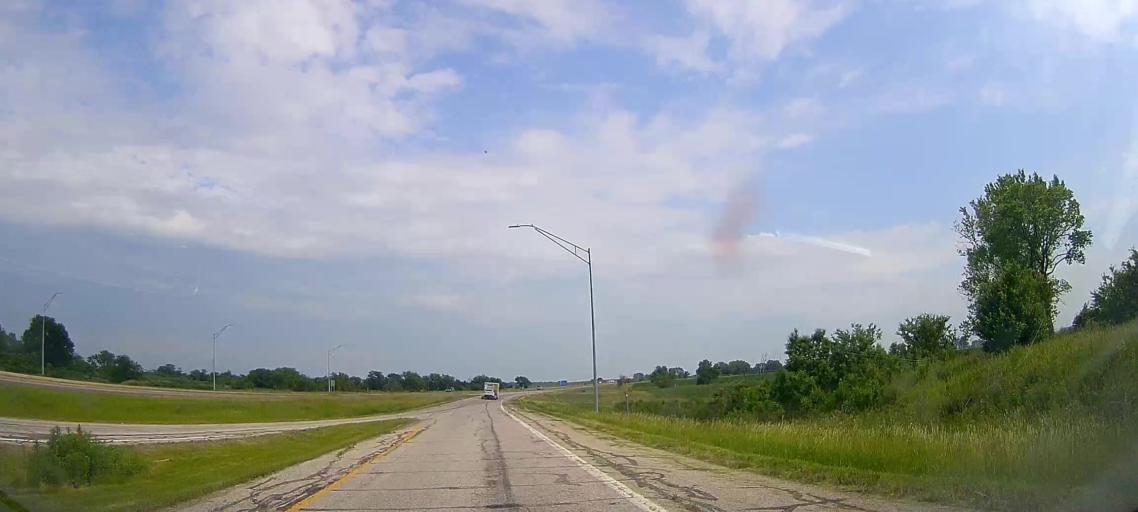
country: US
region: Iowa
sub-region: Monona County
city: Onawa
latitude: 41.9912
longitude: -96.1106
